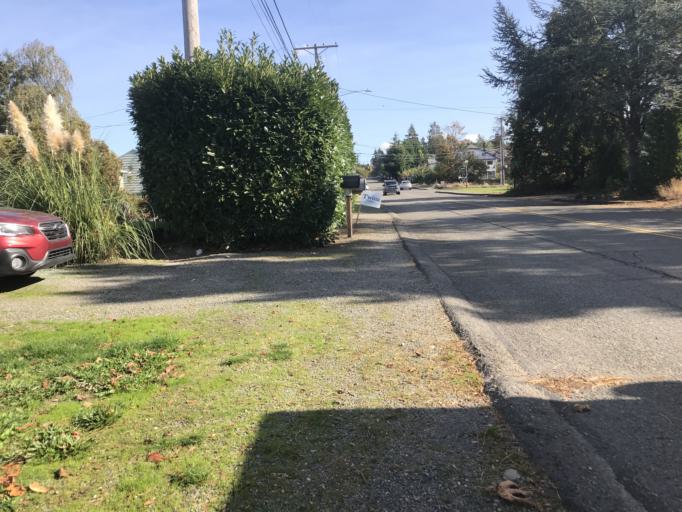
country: US
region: Washington
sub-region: Pierce County
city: University Place
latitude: 47.2427
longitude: -122.5534
